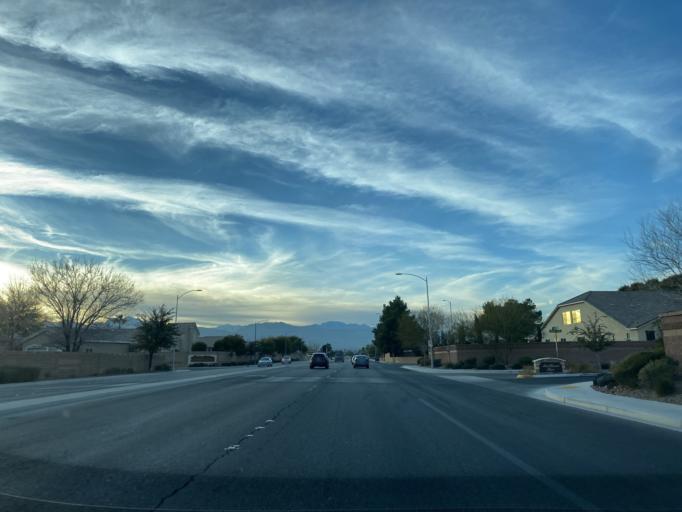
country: US
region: Nevada
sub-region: Clark County
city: Las Vegas
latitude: 36.2615
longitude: -115.2288
